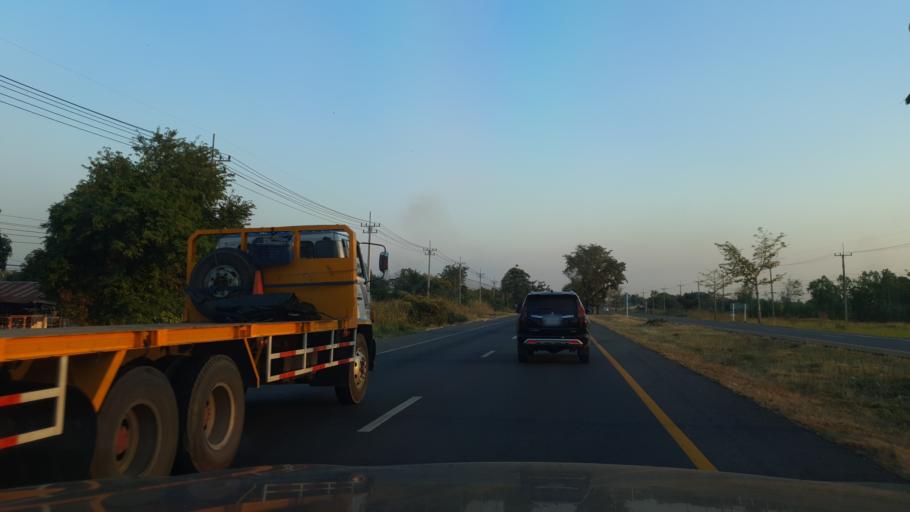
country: TH
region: Nakhon Sawan
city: Banphot Phisai
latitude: 15.8365
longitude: 99.9314
